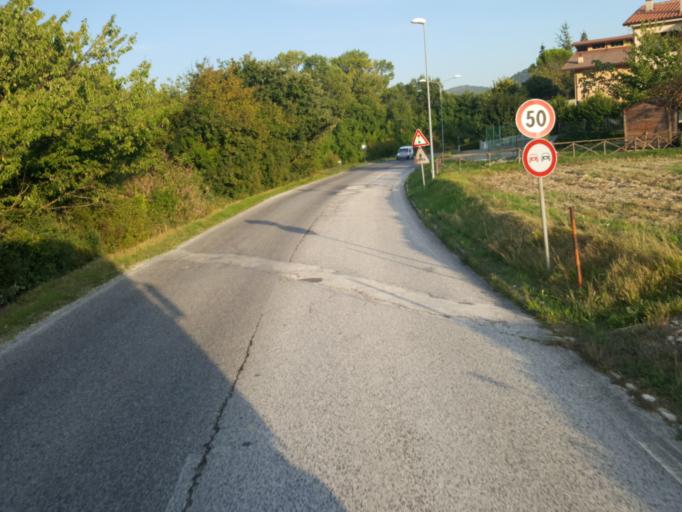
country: IT
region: The Marches
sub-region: Provincia di Ancona
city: Fabriano
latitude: 43.3498
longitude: 12.8357
